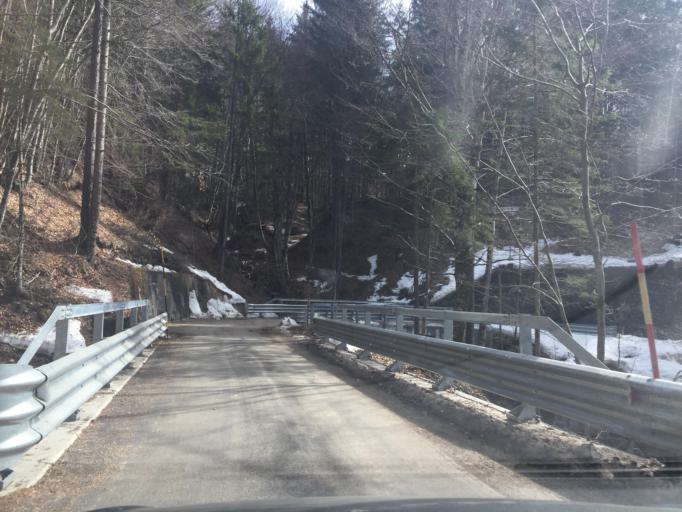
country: IT
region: Friuli Venezia Giulia
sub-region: Provincia di Udine
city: Tarvisio
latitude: 46.5040
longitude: 13.6383
